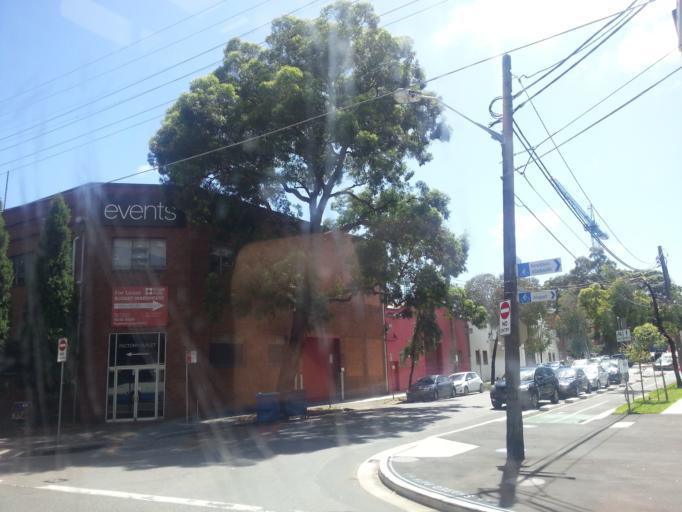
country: AU
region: New South Wales
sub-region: City of Sydney
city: Alexandria
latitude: -33.9029
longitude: 151.2019
